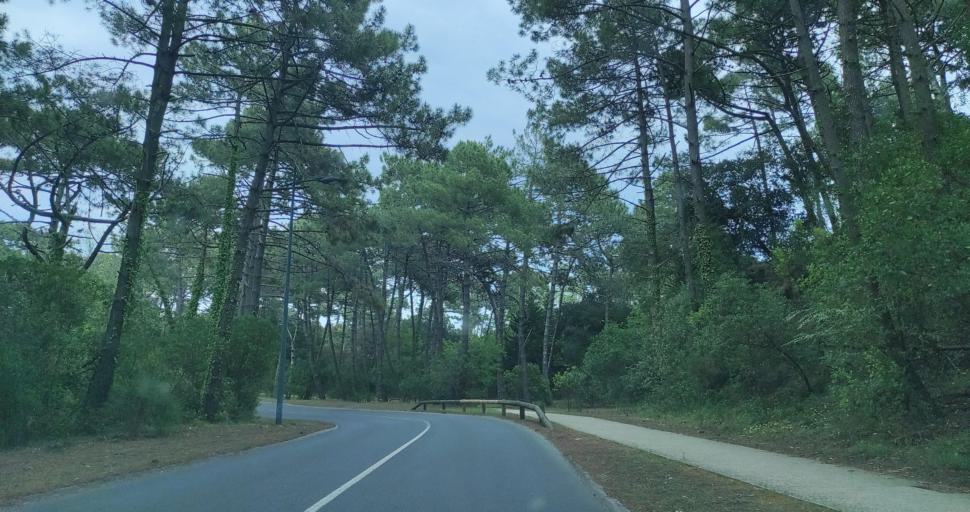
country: FR
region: Aquitaine
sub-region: Departement de la Gironde
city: Arcachon
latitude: 44.6832
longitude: -1.2385
